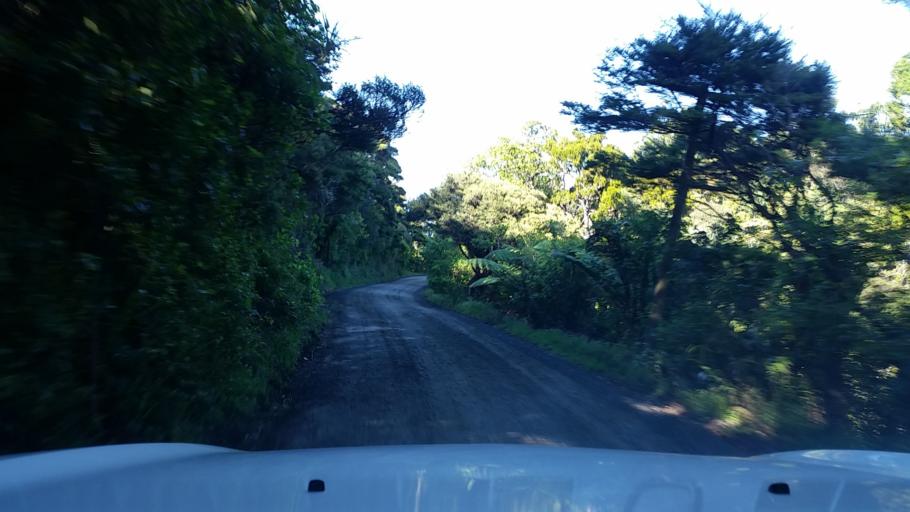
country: NZ
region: Auckland
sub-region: Auckland
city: Titirangi
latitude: -37.0298
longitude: 174.5252
